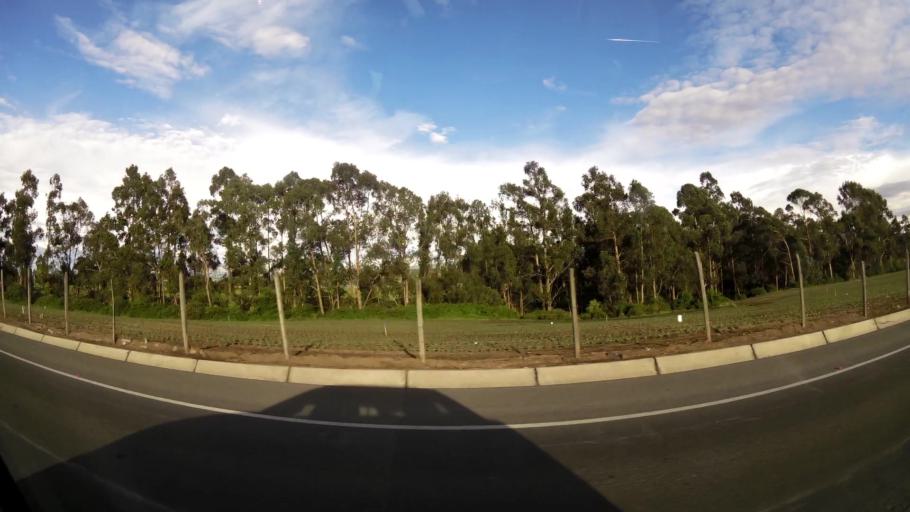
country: EC
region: Cotopaxi
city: Saquisili
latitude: -0.8404
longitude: -78.6192
